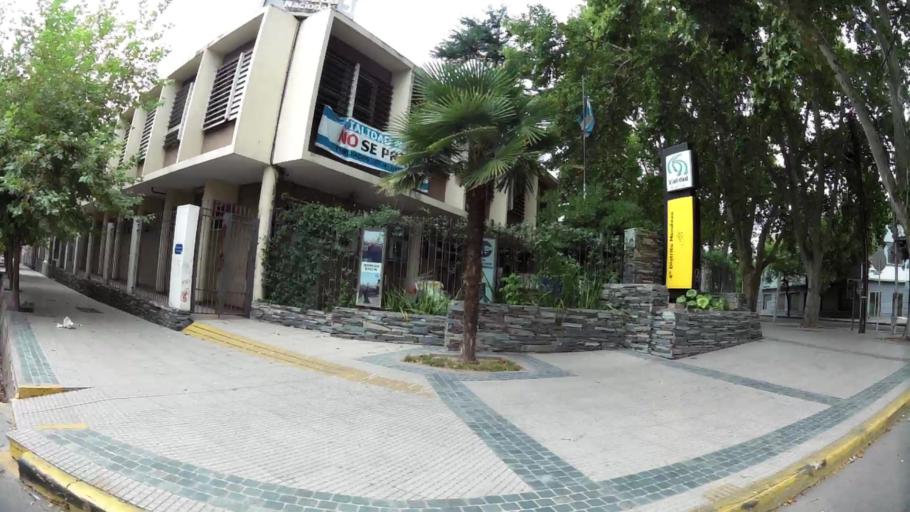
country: AR
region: Mendoza
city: Mendoza
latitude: -32.8962
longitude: -68.8514
